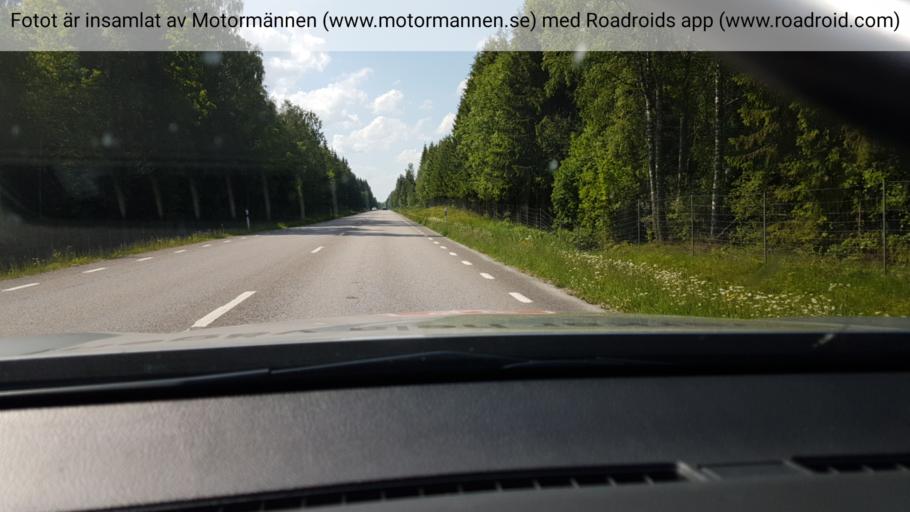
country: SE
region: Vaestra Goetaland
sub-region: Falkopings Kommun
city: Falkoeping
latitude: 58.0437
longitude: 13.5480
